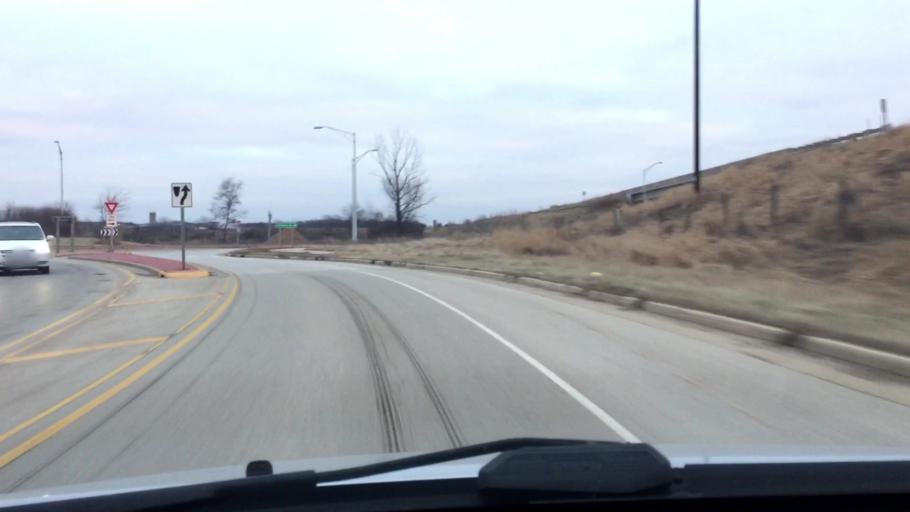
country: US
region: Wisconsin
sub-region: Jefferson County
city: Watertown
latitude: 43.1584
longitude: -88.7494
